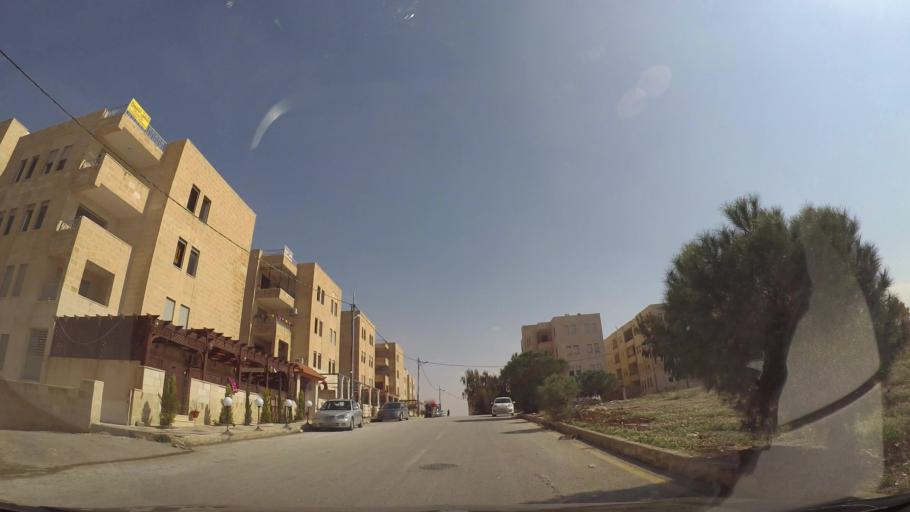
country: JO
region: Zarqa
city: Zarqa
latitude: 32.0754
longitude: 36.1115
